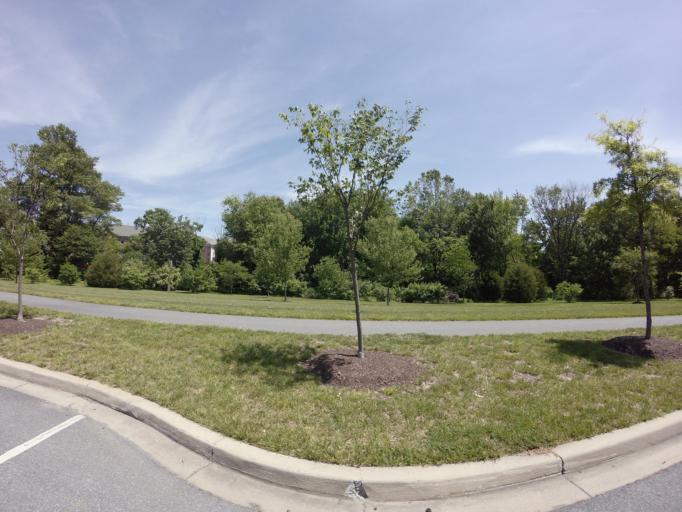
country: US
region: Maryland
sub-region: Frederick County
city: Urbana
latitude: 39.3352
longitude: -77.3376
